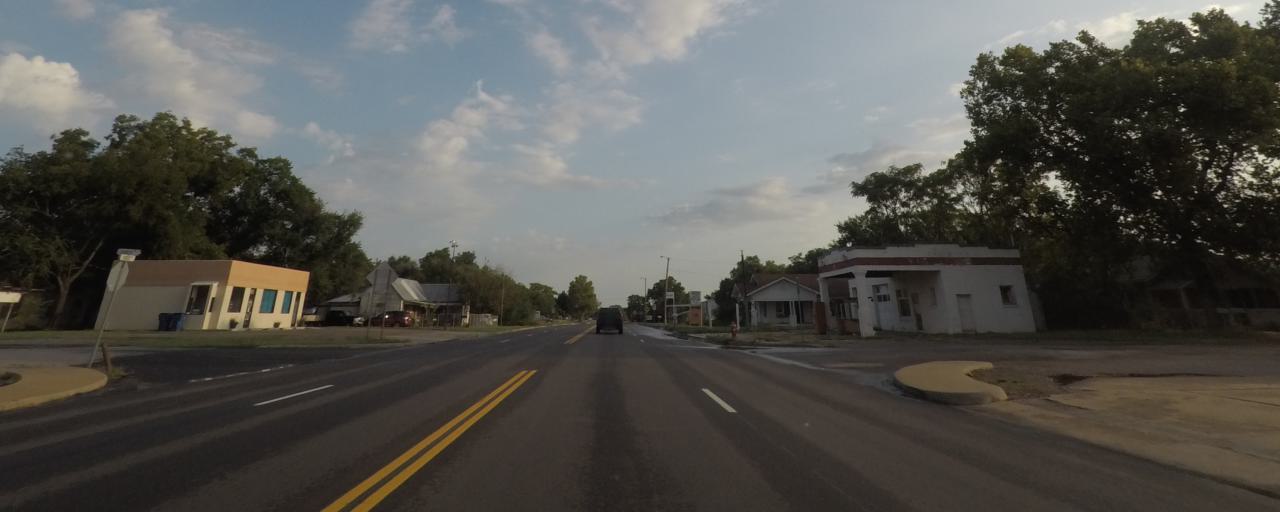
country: US
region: Oklahoma
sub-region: Stephens County
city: Comanche
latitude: 34.3698
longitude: -97.9642
